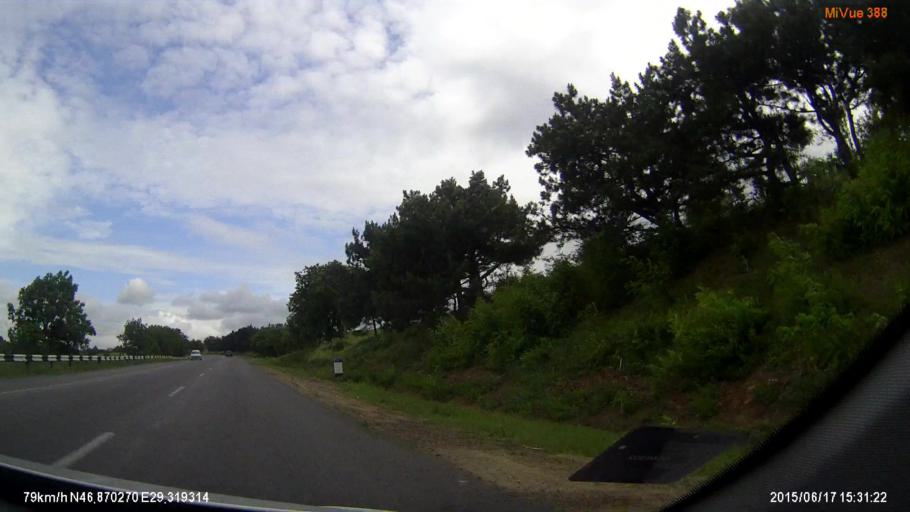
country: MD
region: Anenii Noi
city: Anenii Noi
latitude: 46.8705
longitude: 29.3192
